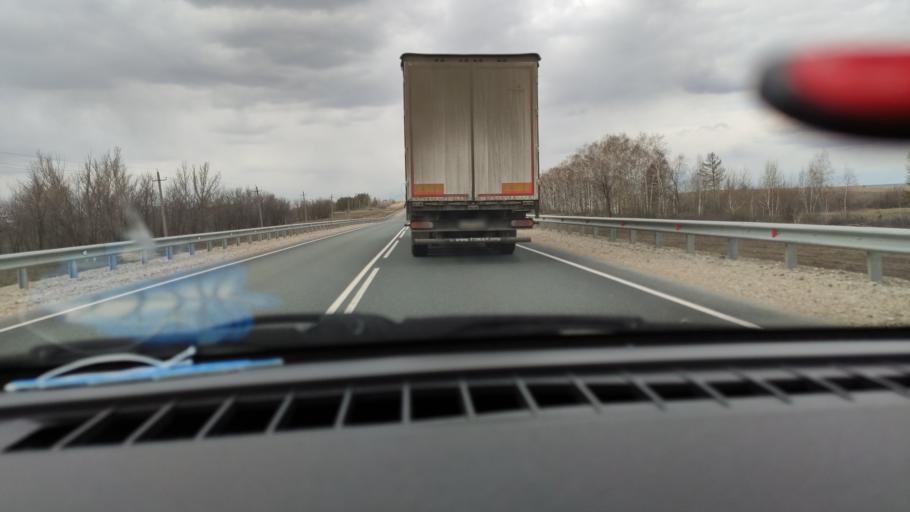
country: RU
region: Saratov
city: Shikhany
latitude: 52.1610
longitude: 47.1212
